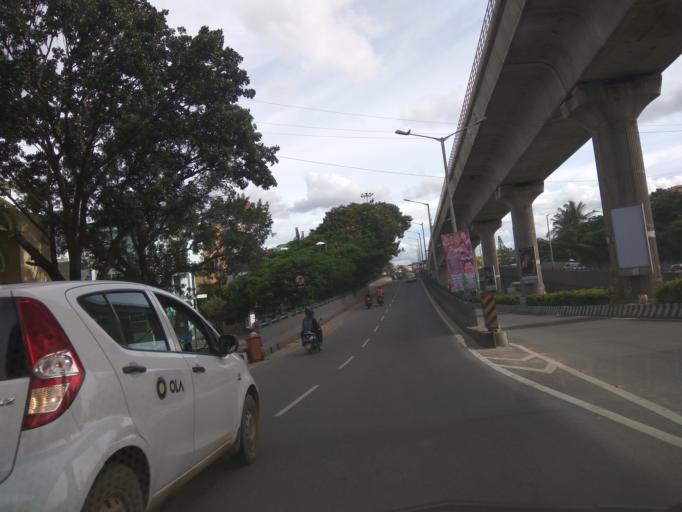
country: IN
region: Karnataka
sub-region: Bangalore Urban
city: Bangalore
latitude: 13.0052
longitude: 77.5490
